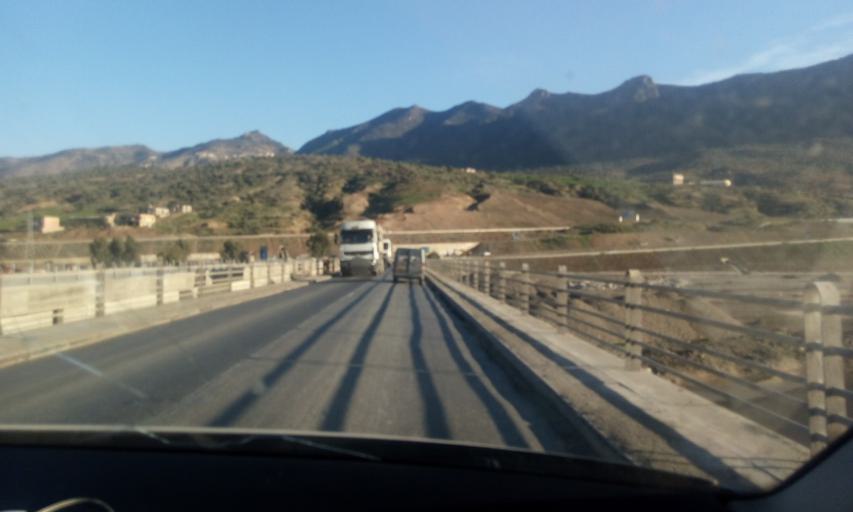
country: DZ
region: Bejaia
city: Akbou
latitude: 36.4817
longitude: 4.5913
